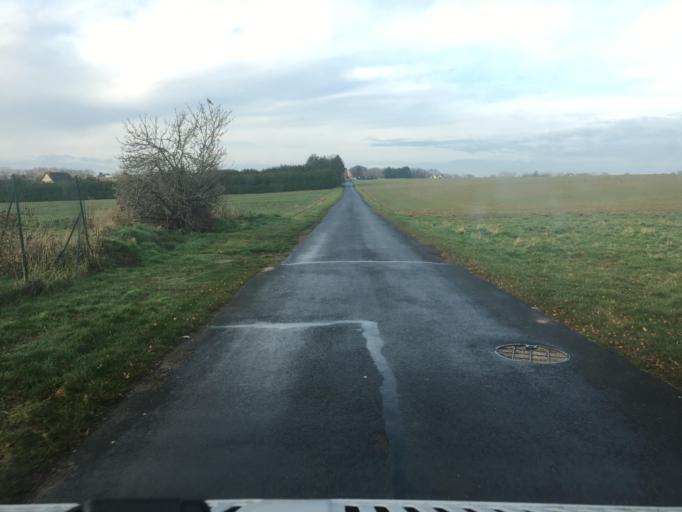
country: FR
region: Lower Normandy
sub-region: Departement du Calvados
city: Rots
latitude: 49.2045
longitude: -0.4675
